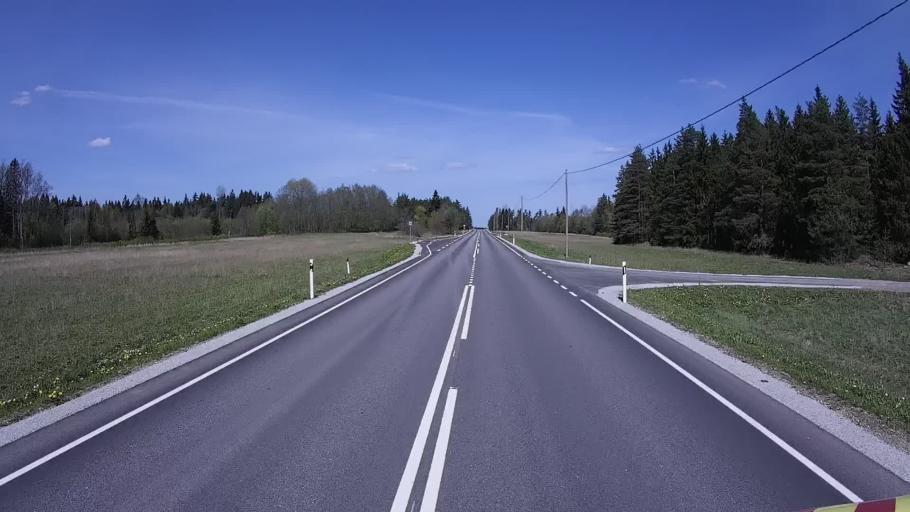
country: EE
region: Harju
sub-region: Paldiski linn
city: Paldiski
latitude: 59.1996
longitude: 24.0972
